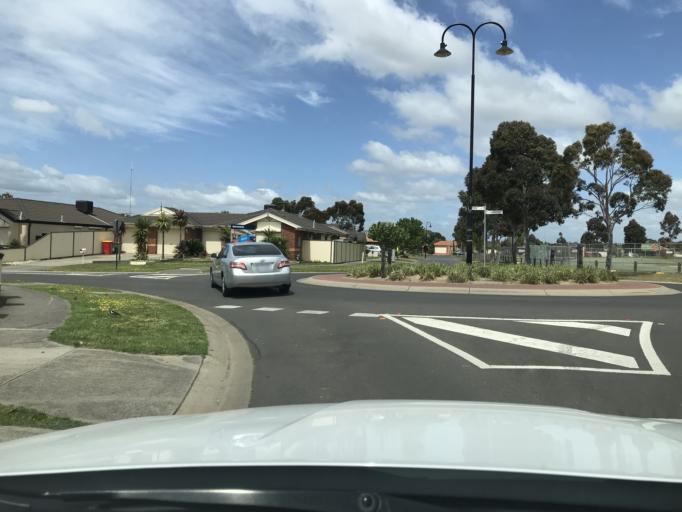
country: AU
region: Victoria
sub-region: Hume
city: Roxburgh Park
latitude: -37.6142
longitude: 144.9357
